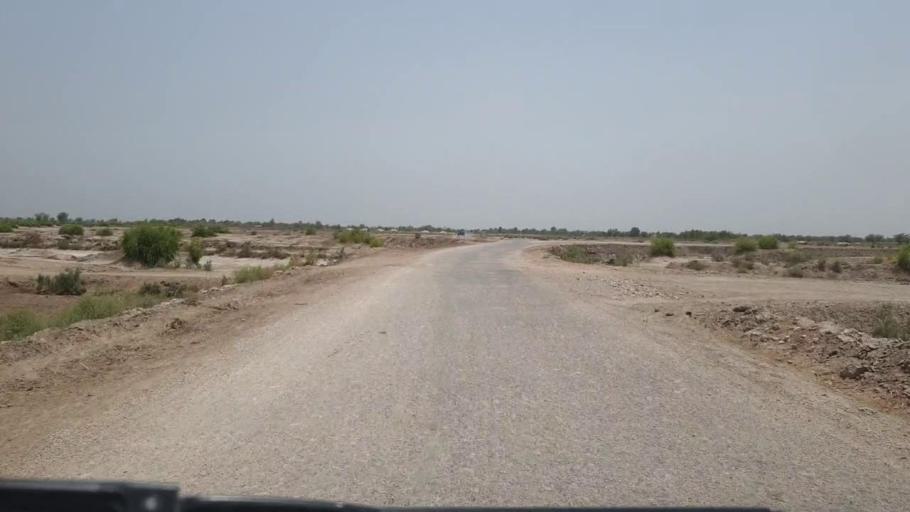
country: PK
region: Sindh
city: Daulatpur
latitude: 26.4572
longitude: 68.1185
